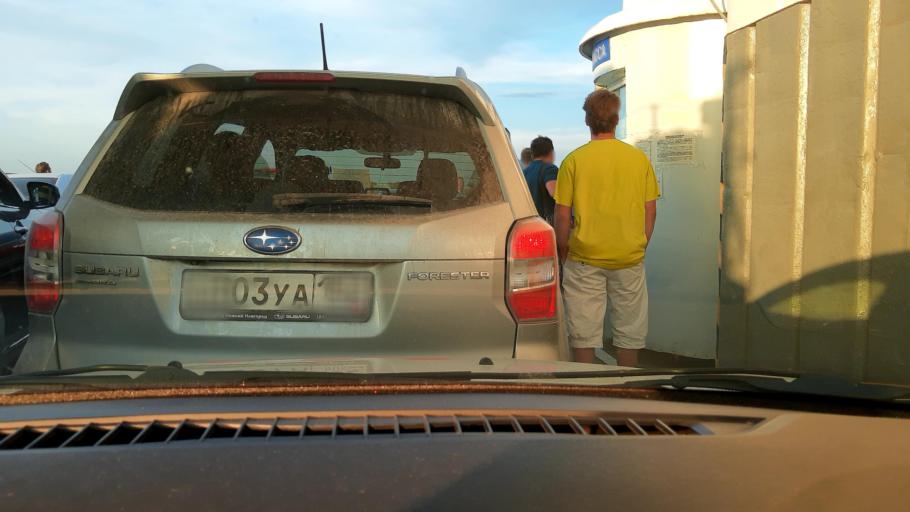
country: RU
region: Nizjnij Novgorod
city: Nizhniy Novgorod
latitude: 56.3379
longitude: 44.0321
